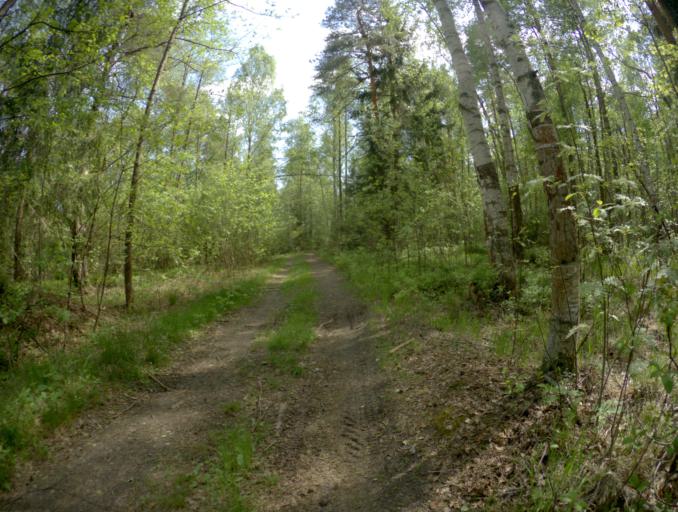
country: RU
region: Vladimir
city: Ivanishchi
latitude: 55.6742
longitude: 40.3929
